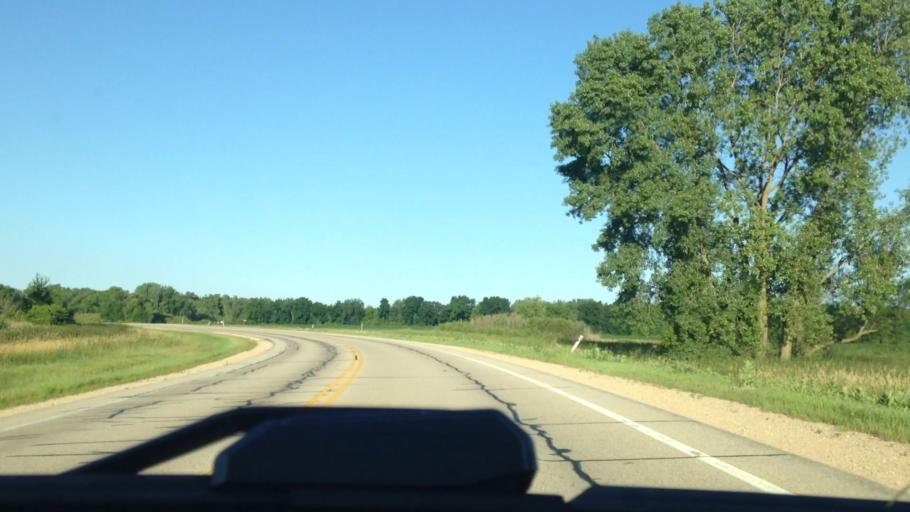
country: US
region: Wisconsin
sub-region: Columbia County
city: Rio
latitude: 43.3400
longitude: -89.2538
